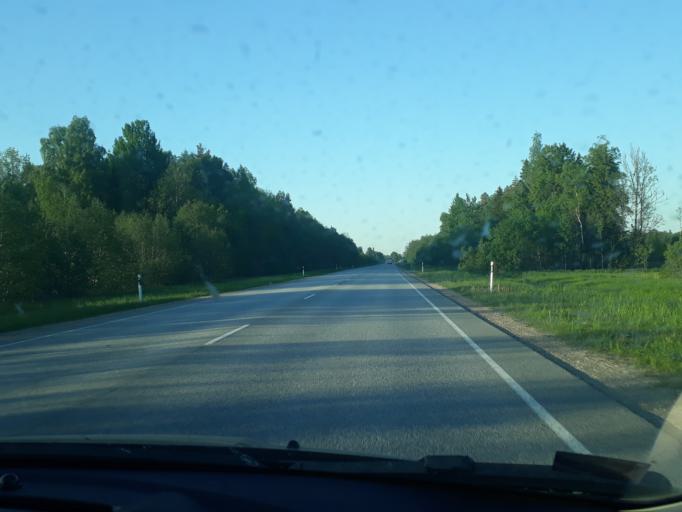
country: EE
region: Paernumaa
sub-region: Sindi linn
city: Sindi
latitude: 58.4694
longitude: 24.7116
